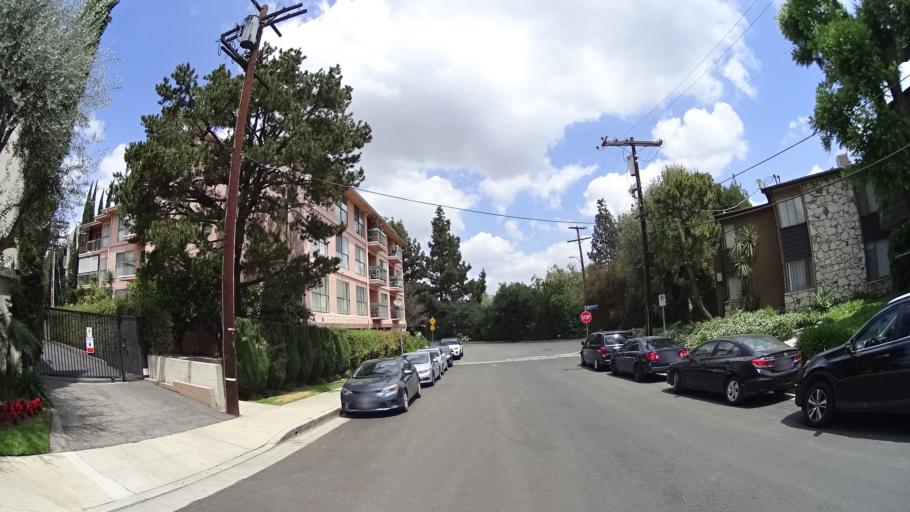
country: US
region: California
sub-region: Los Angeles County
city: Sherman Oaks
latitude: 34.1470
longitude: -118.4184
